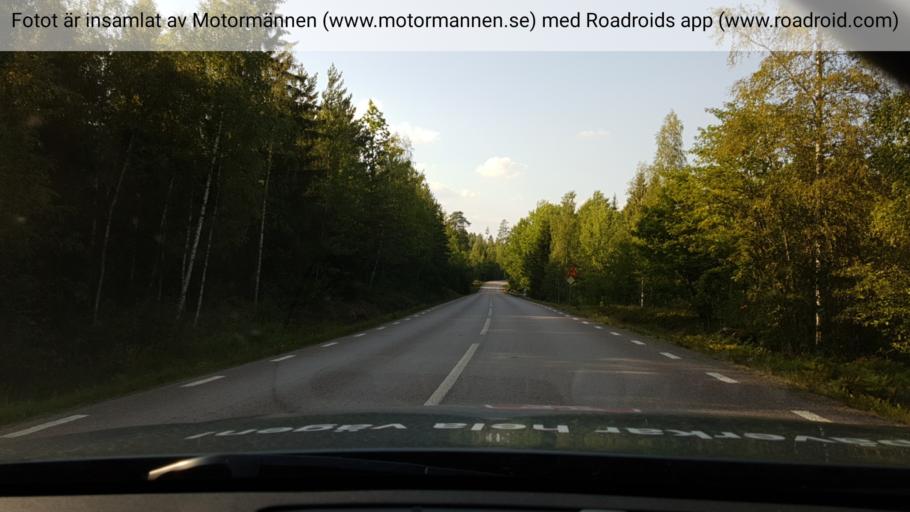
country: SE
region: Soedermanland
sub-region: Strangnas Kommun
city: Mariefred
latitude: 59.1829
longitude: 17.1896
